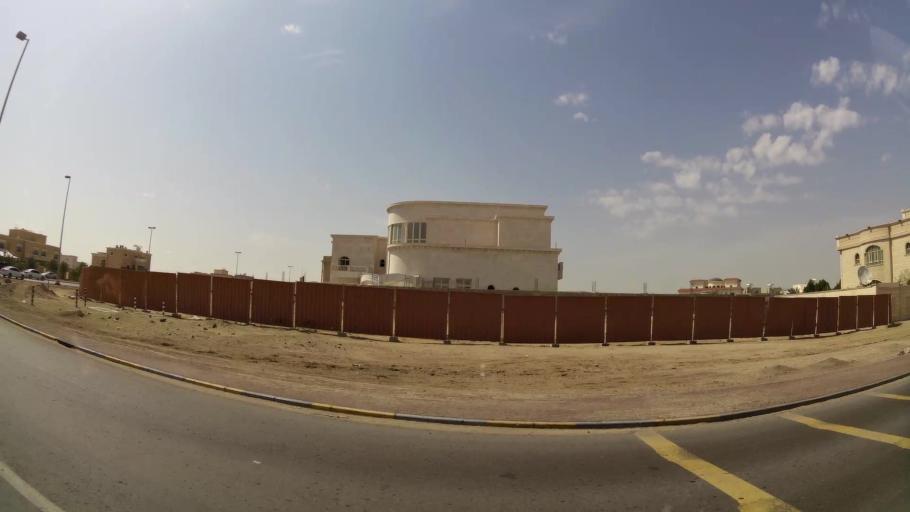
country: AE
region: Abu Dhabi
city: Abu Dhabi
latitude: 24.3172
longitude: 54.5746
